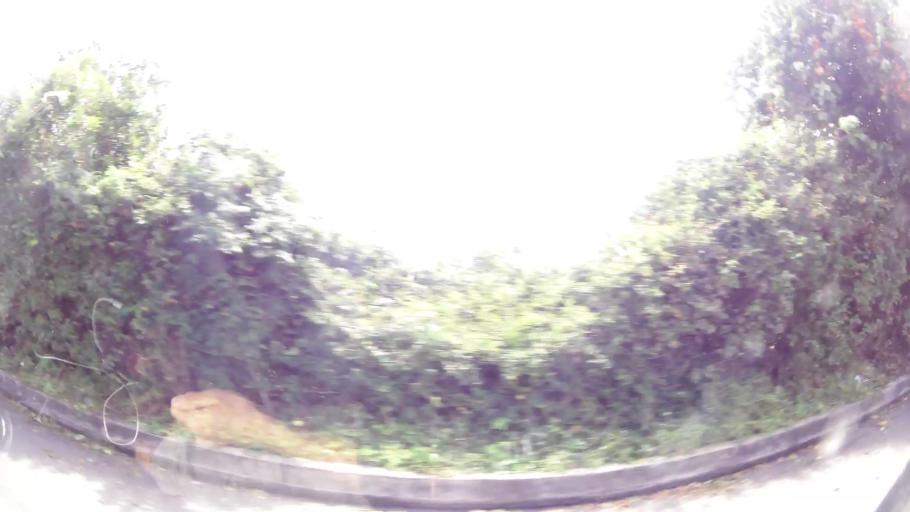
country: EC
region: Pichincha
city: Quito
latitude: -0.2176
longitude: -78.4319
